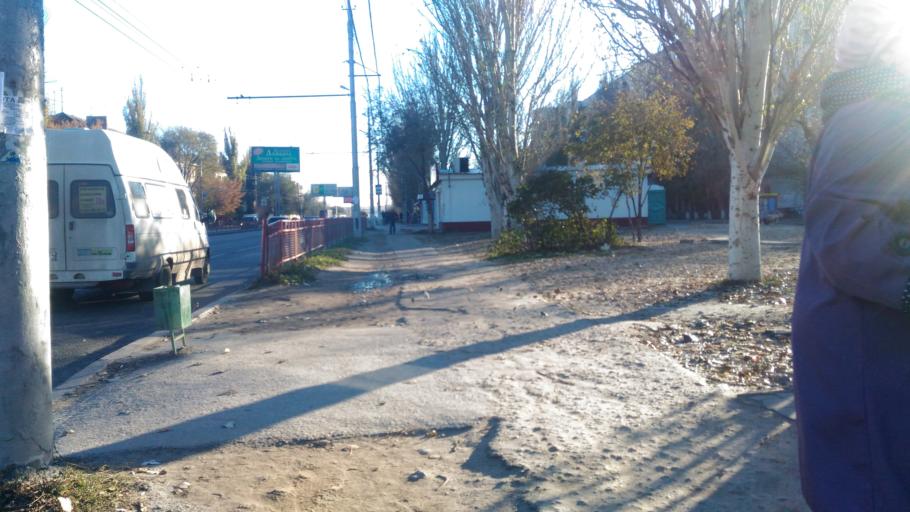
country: RU
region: Volgograd
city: Volgograd
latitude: 48.6018
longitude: 44.4215
